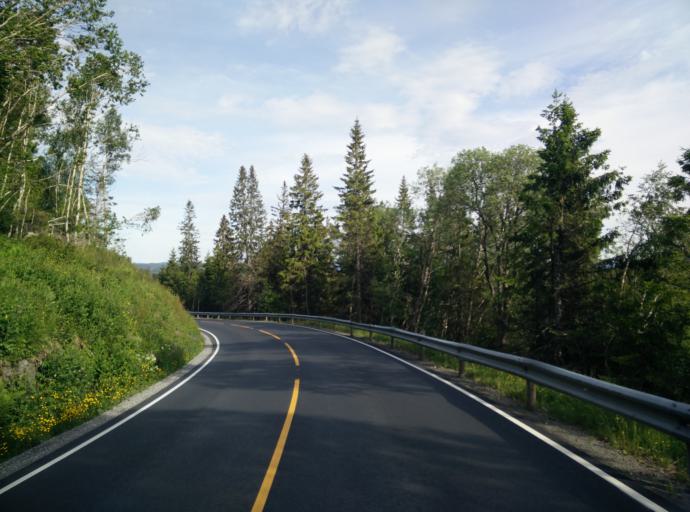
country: NO
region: Sor-Trondelag
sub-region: Snillfjord
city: Krokstadora
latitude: 63.2307
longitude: 9.5670
